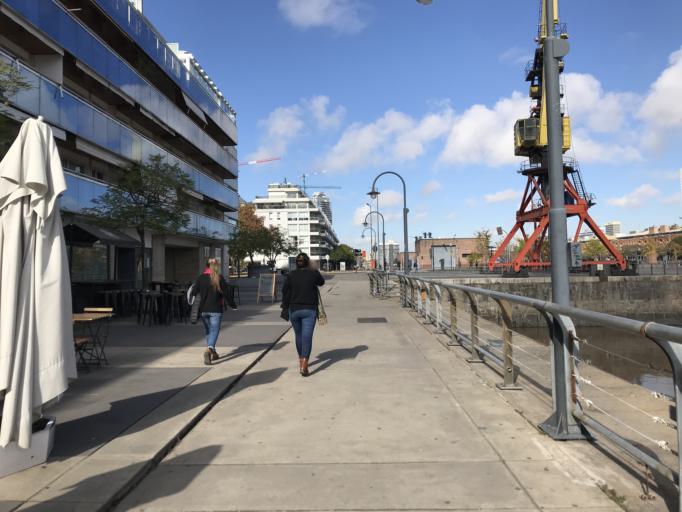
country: AR
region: Buenos Aires F.D.
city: Buenos Aires
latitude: -34.6112
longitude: -58.3638
